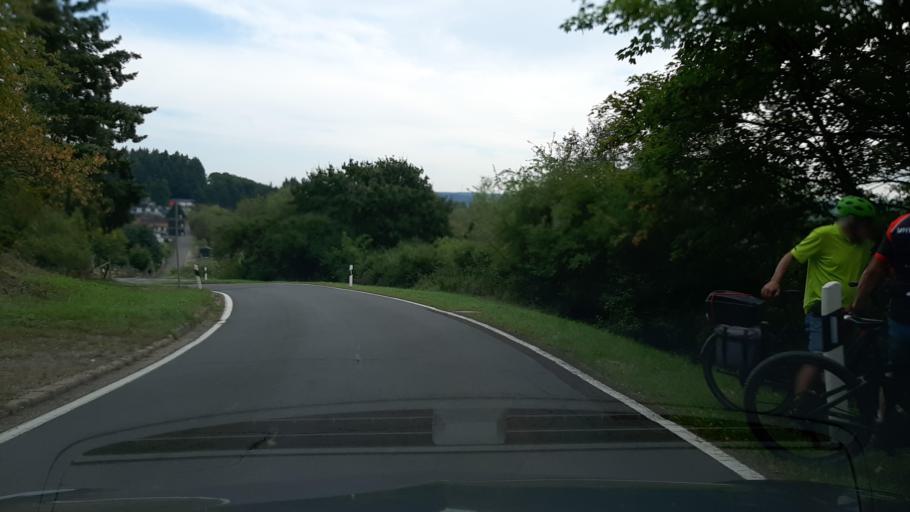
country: DE
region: Rheinland-Pfalz
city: Krov
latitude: 49.9895
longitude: 7.0957
